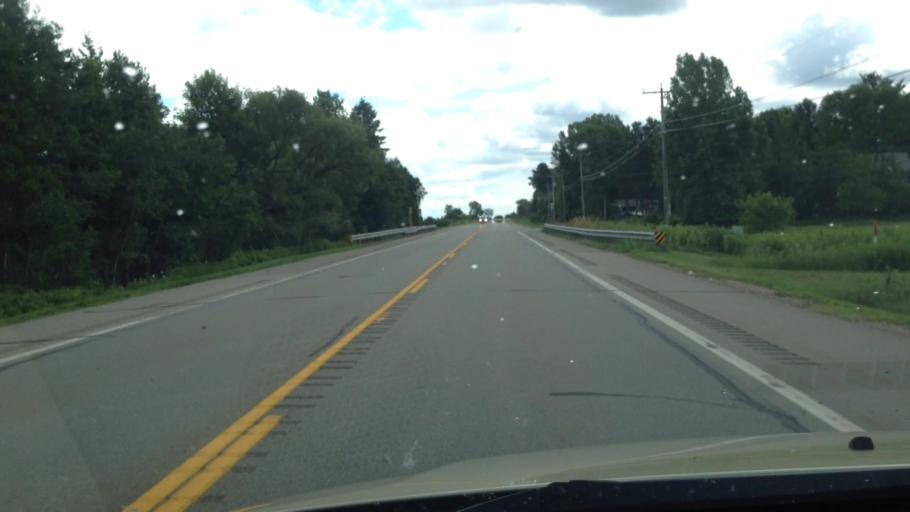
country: US
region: Michigan
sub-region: Menominee County
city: Menominee
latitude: 45.2028
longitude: -87.5368
